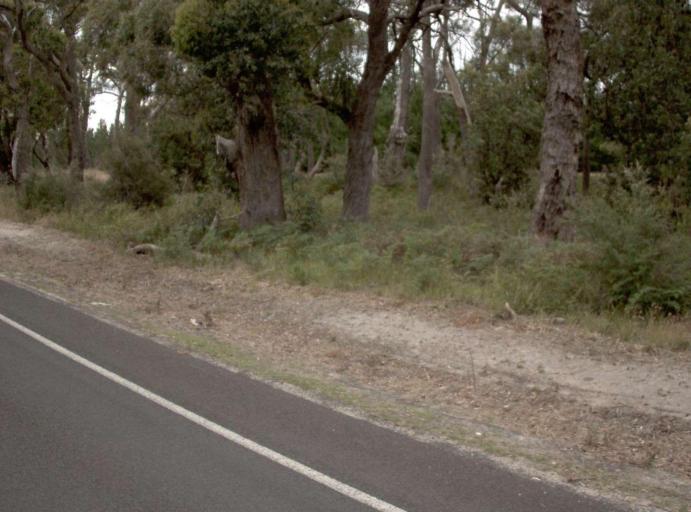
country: AU
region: Victoria
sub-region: Wellington
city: Sale
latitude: -38.2297
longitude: 147.0549
